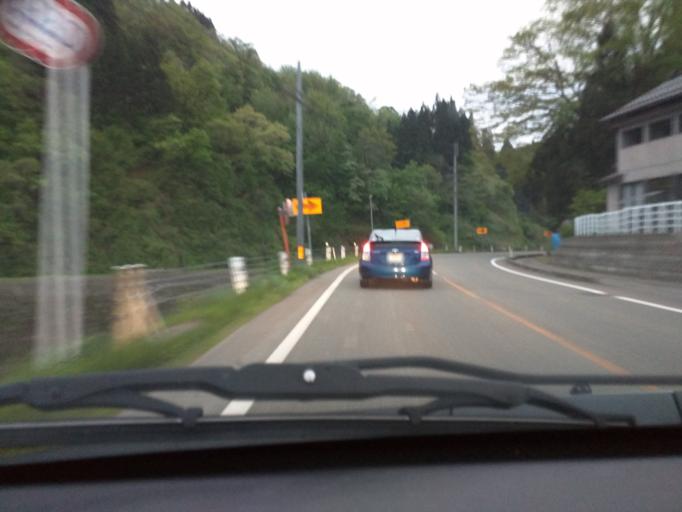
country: JP
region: Niigata
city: Ojiya
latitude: 37.3190
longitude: 138.7027
